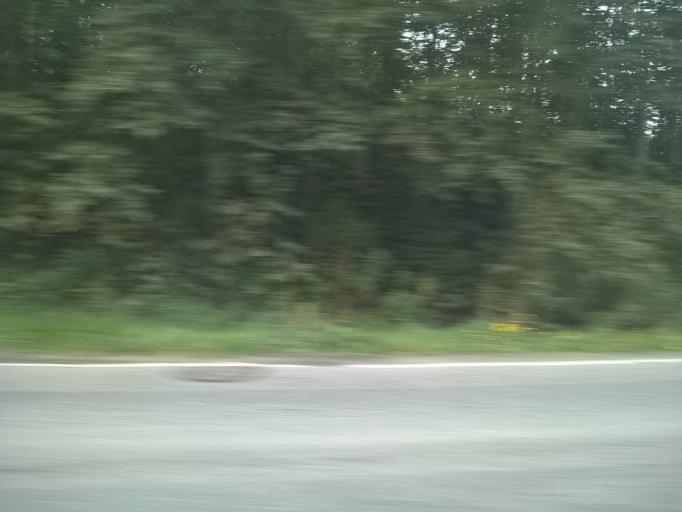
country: FI
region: Pirkanmaa
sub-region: Tampere
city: Tampere
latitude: 61.4881
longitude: 23.8244
